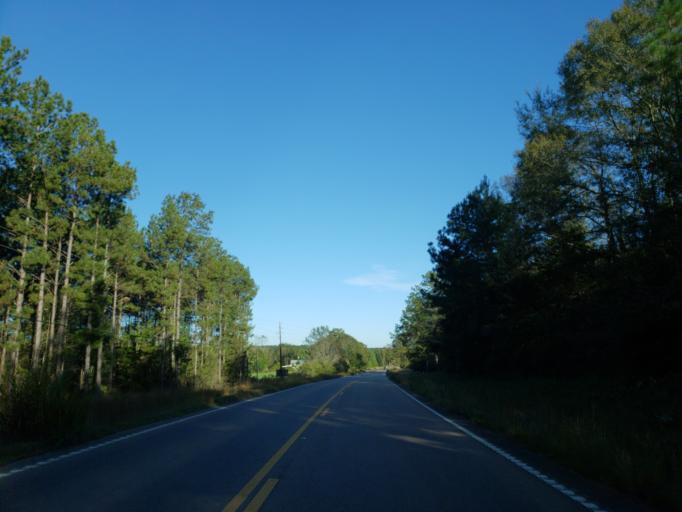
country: US
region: Mississippi
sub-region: Perry County
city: Richton
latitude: 31.3760
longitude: -88.8513
